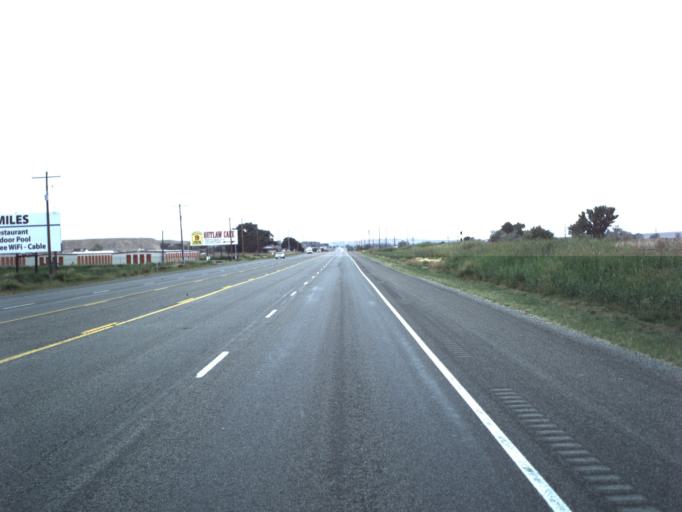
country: US
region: Utah
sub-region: Carbon County
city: Wellington
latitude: 39.5650
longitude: -110.7732
